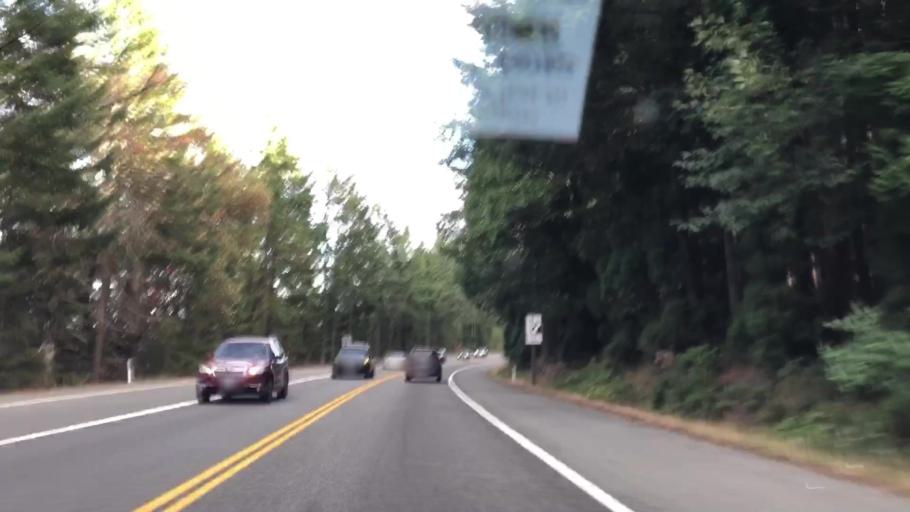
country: CA
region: British Columbia
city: Langford
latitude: 48.5774
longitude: -123.5281
